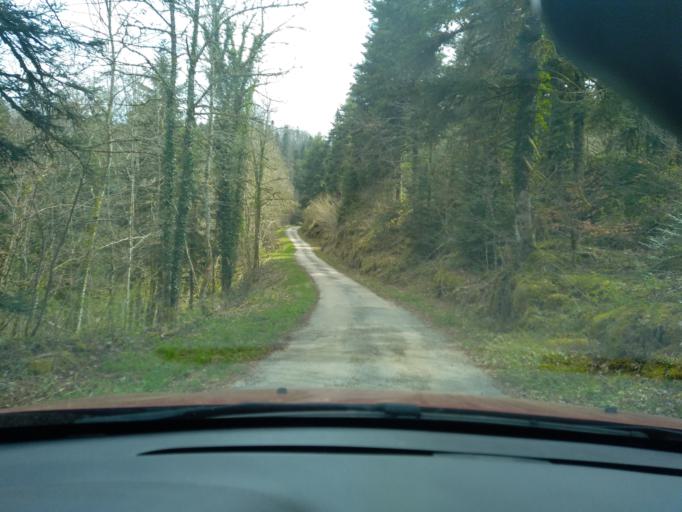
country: FR
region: Franche-Comte
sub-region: Departement du Jura
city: Moirans-en-Montagne
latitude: 46.4742
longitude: 5.7564
